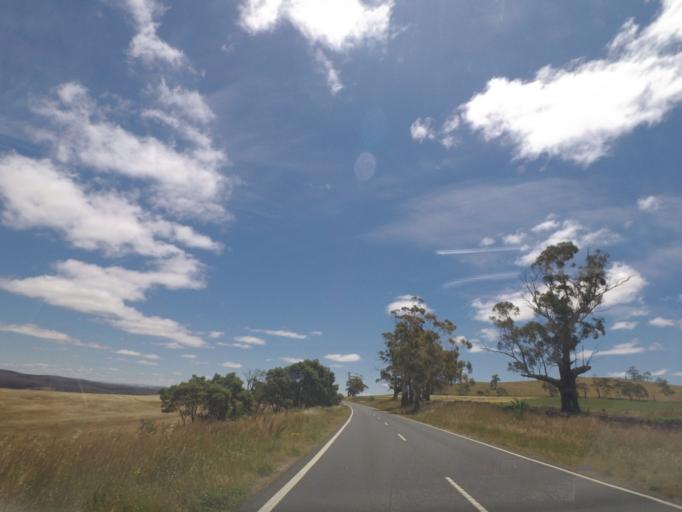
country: AU
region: Victoria
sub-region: Mount Alexander
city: Castlemaine
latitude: -37.2718
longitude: 144.1449
